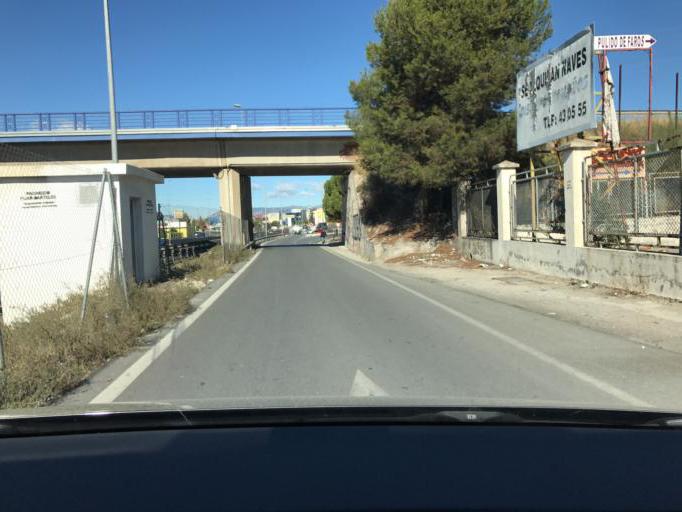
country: ES
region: Andalusia
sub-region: Provincia de Granada
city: Peligros
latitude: 37.2210
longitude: -3.6293
